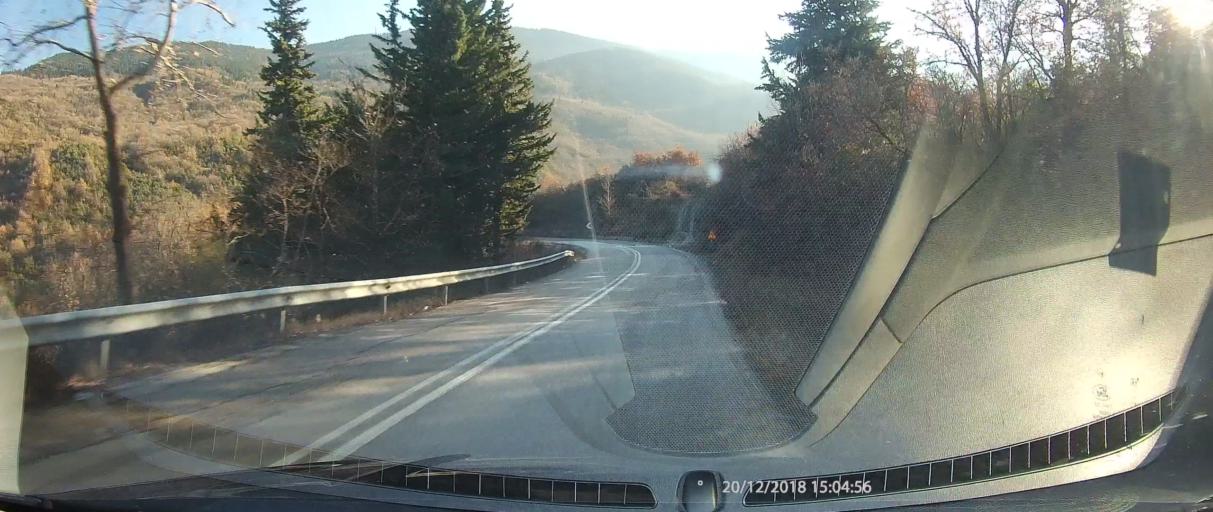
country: GR
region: Central Greece
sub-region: Nomos Evrytanias
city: Karpenisi
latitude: 38.9101
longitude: 21.9278
